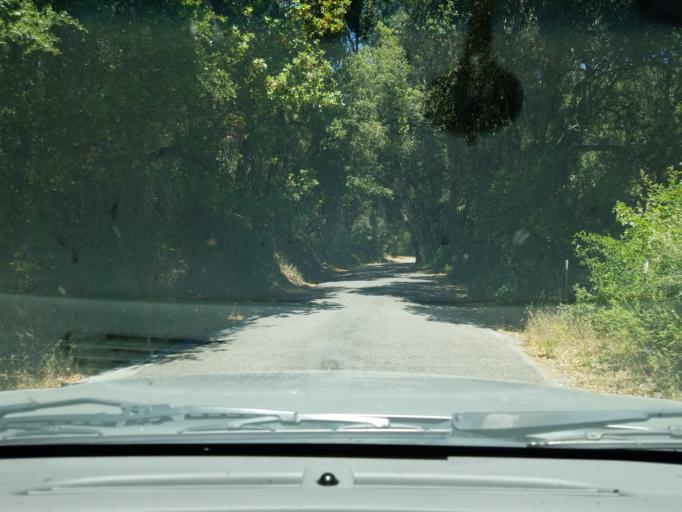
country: US
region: California
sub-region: Monterey County
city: Gonzales
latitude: 36.3557
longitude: -121.5480
